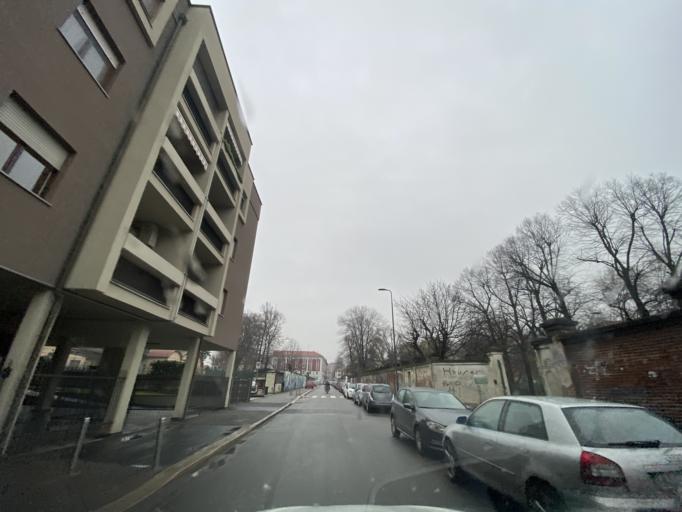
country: IT
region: Lombardy
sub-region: Citta metropolitana di Milano
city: Milano
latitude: 45.4982
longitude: 9.1759
